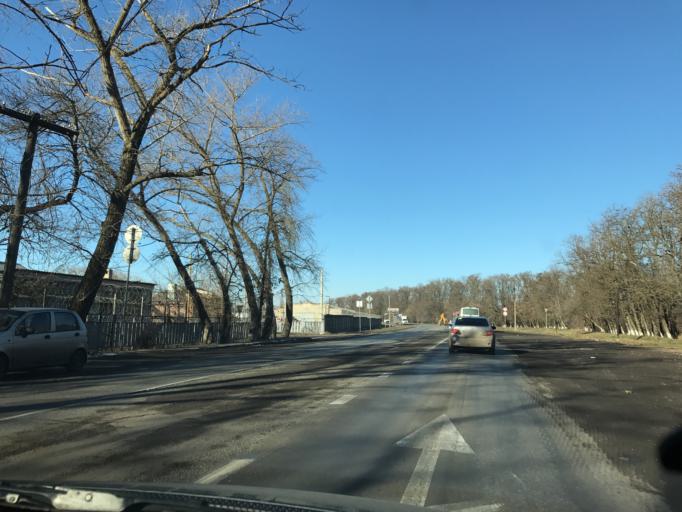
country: RU
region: Rostov
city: Kirovskaya
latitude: 46.9796
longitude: 40.0425
